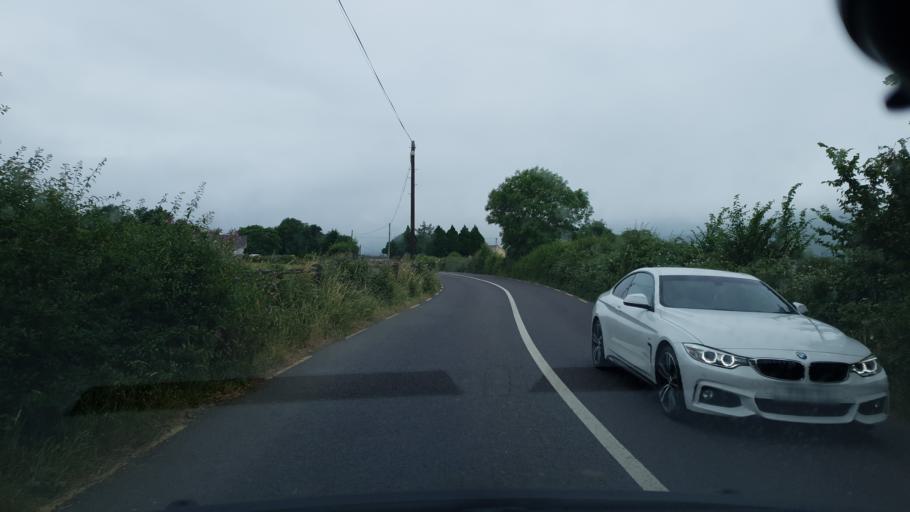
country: IE
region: Munster
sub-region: Ciarrai
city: Tralee
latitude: 52.1613
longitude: -9.6887
